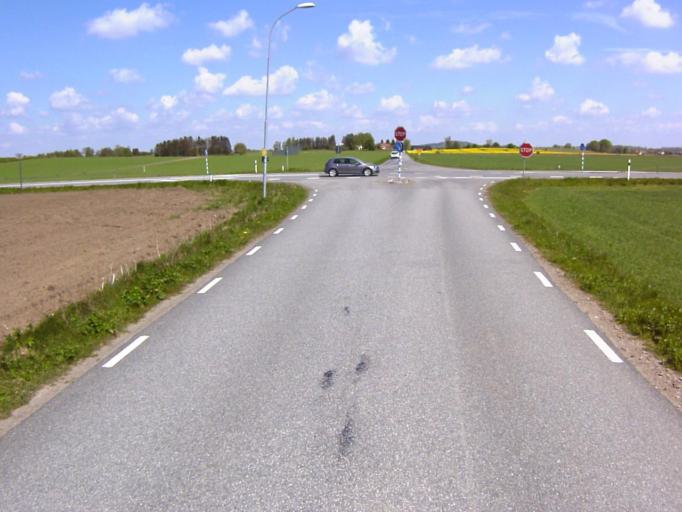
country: SE
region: Skane
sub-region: Kristianstads Kommun
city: Fjalkinge
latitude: 56.0158
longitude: 14.2426
